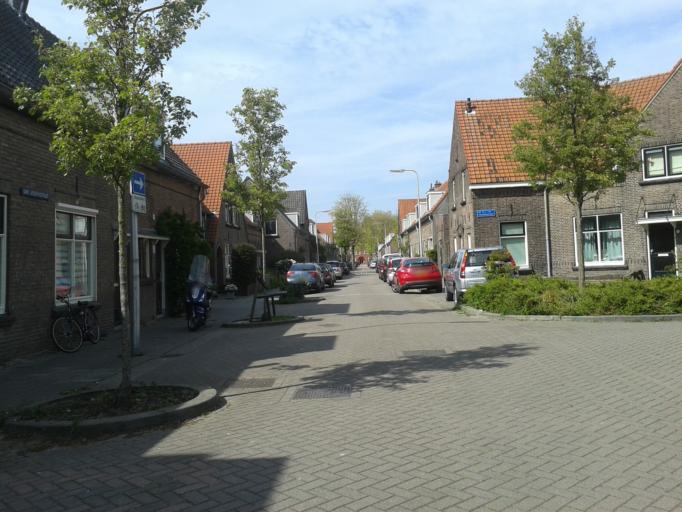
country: NL
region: South Holland
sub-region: Gemeente Gouda
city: Gouda
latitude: 52.0106
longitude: 4.7192
